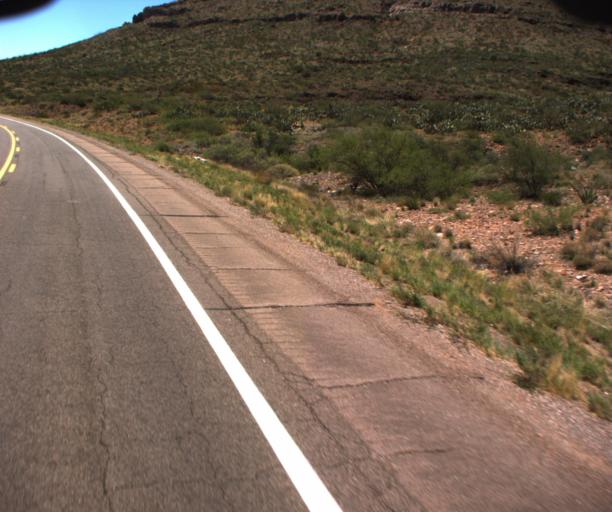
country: US
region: Arizona
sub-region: Greenlee County
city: Clifton
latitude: 32.8481
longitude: -109.3487
